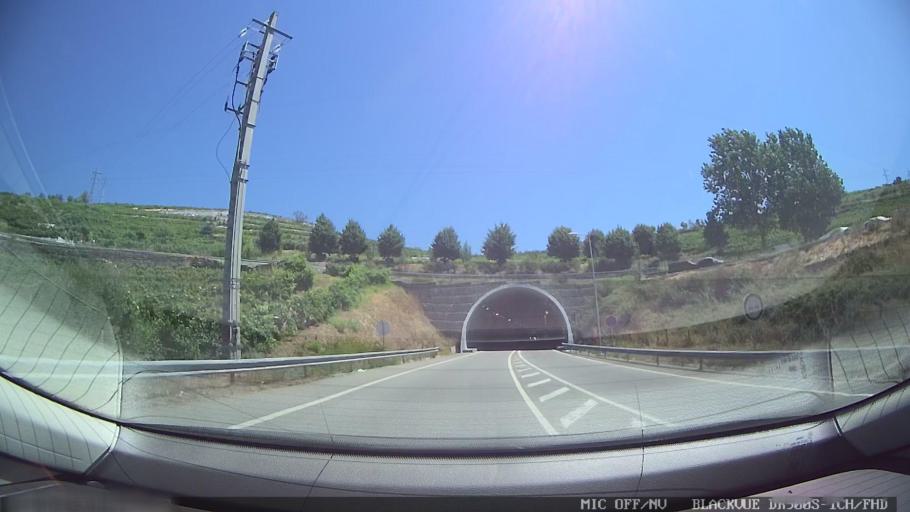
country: PT
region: Vila Real
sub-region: Peso da Regua
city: Peso da Regua
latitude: 41.1697
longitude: -7.7793
